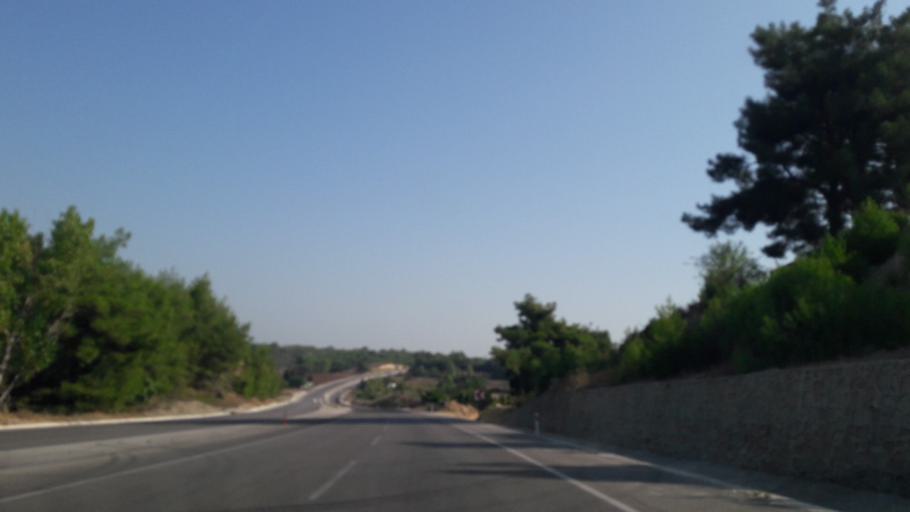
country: TR
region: Adana
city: Sagkaya
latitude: 37.1729
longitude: 35.5640
